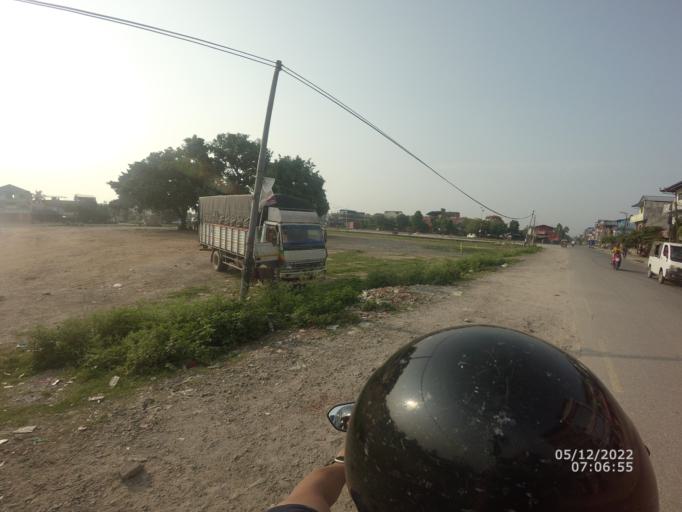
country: NP
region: Central Region
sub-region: Narayani Zone
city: Bharatpur
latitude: 27.6699
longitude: 84.4385
